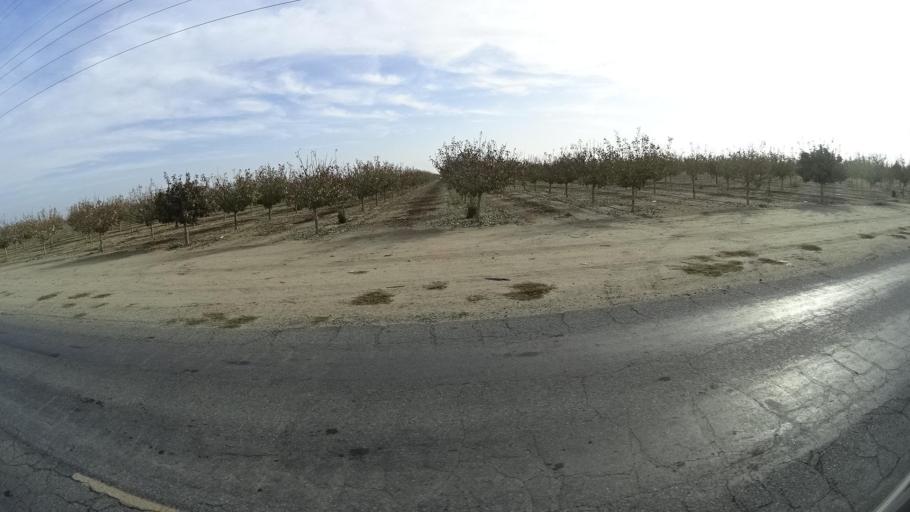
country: US
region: California
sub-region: Kern County
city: Delano
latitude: 35.7552
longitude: -119.2053
